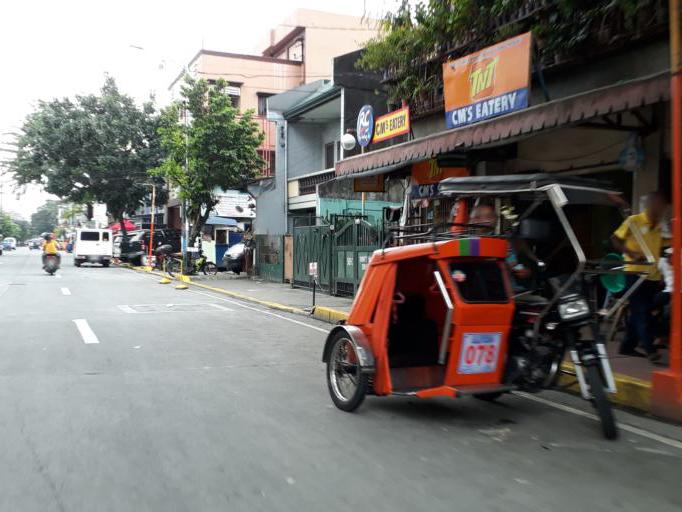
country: PH
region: Metro Manila
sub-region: City of Manila
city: Manila
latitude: 14.6085
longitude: 120.9982
